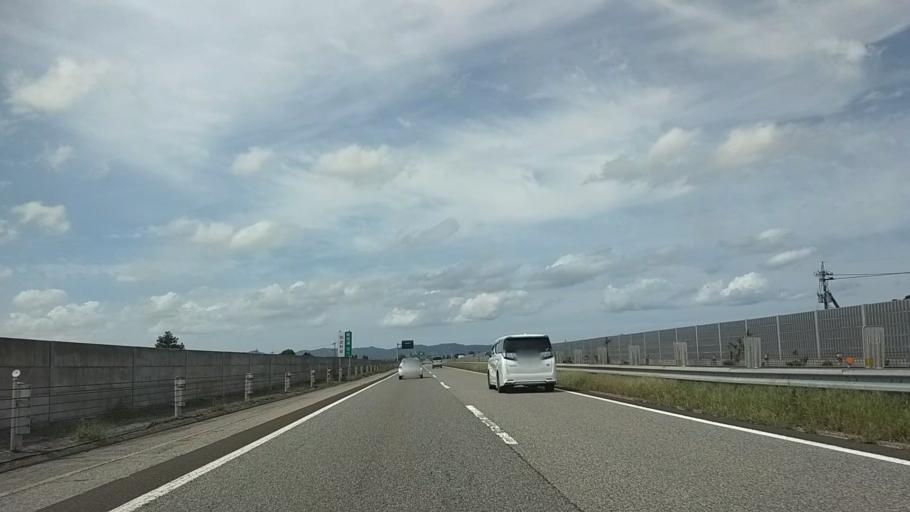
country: JP
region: Toyama
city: Nanto-shi
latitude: 36.6253
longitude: 136.9284
